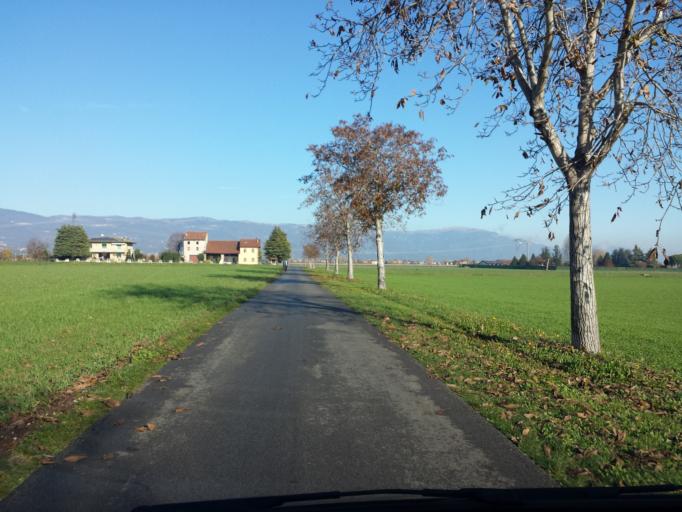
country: IT
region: Veneto
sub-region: Provincia di Vicenza
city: Sandrigo
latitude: 45.6729
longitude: 11.5936
